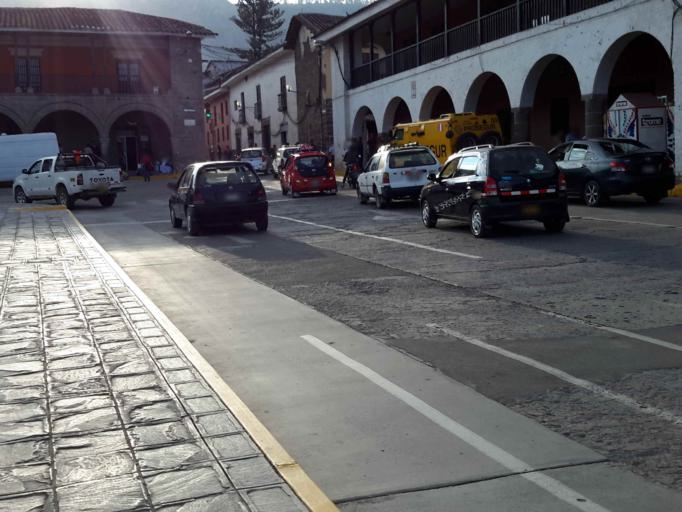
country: PE
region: Ayacucho
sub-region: Provincia de Huamanga
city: Ayacucho
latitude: -13.1598
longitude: -74.2259
